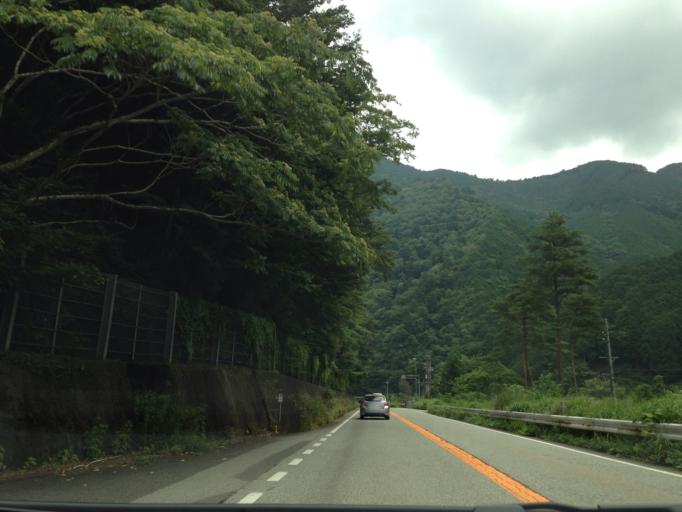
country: JP
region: Gifu
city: Gujo
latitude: 35.7528
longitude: 137.2263
